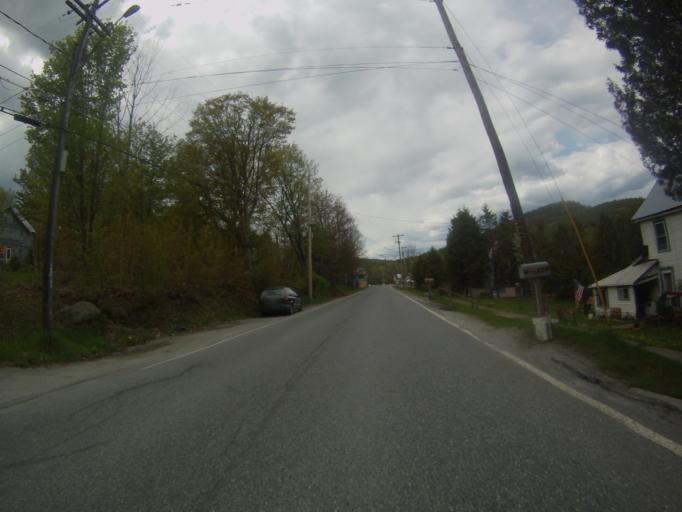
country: US
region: New York
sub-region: Essex County
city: Mineville
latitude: 44.0856
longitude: -73.5313
